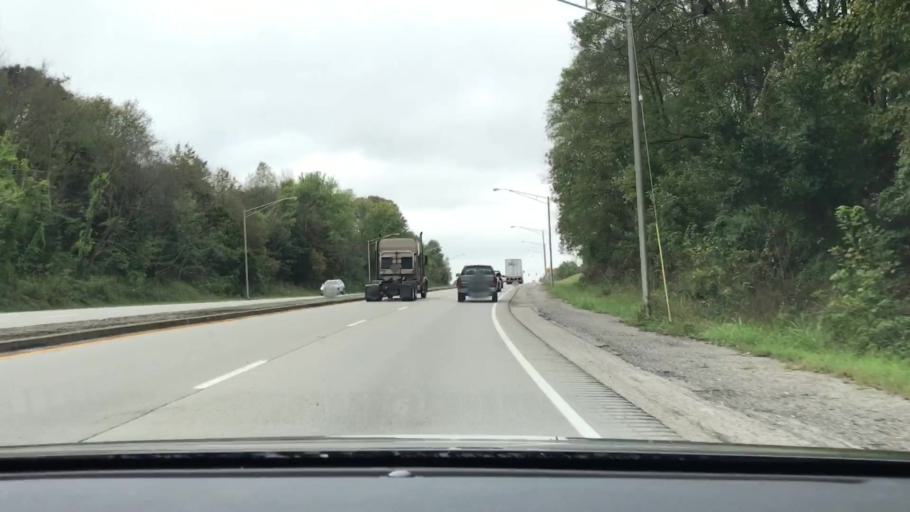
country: US
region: Kentucky
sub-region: Pulaski County
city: Somerset
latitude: 37.0929
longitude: -84.6253
